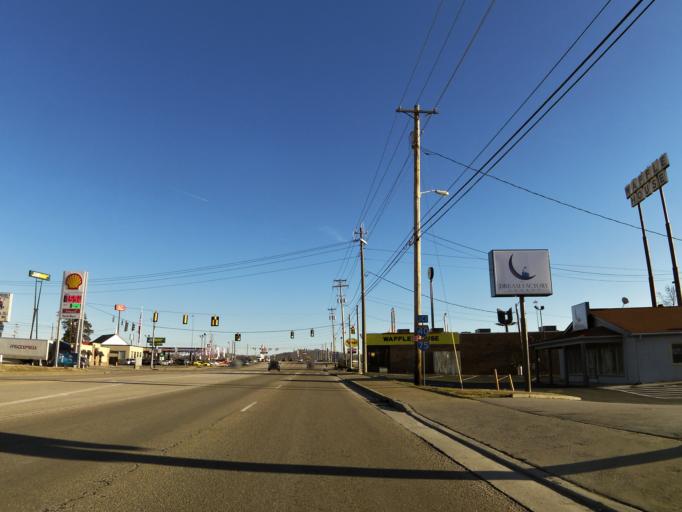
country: US
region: Tennessee
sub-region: Knox County
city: Farragut
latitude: 35.9080
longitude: -84.1478
